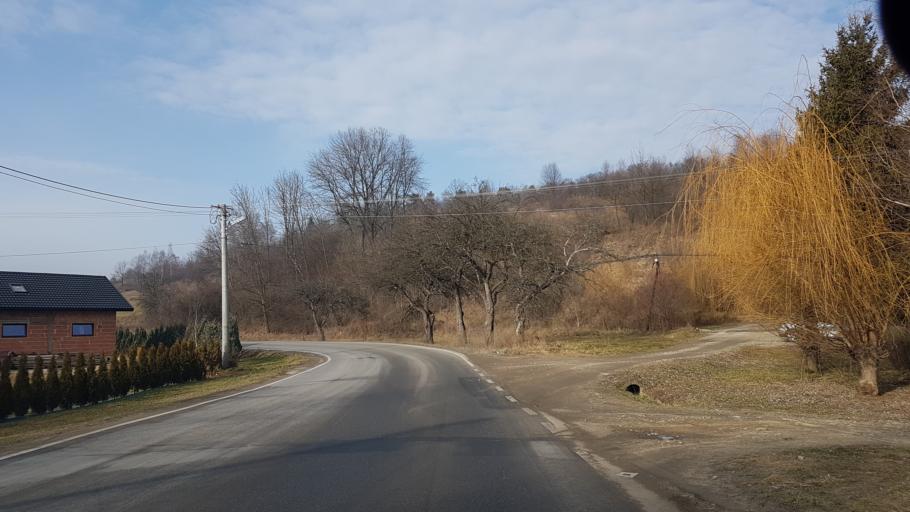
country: PL
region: Lesser Poland Voivodeship
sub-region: Powiat nowosadecki
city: Podegrodzie
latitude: 49.5609
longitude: 20.5729
